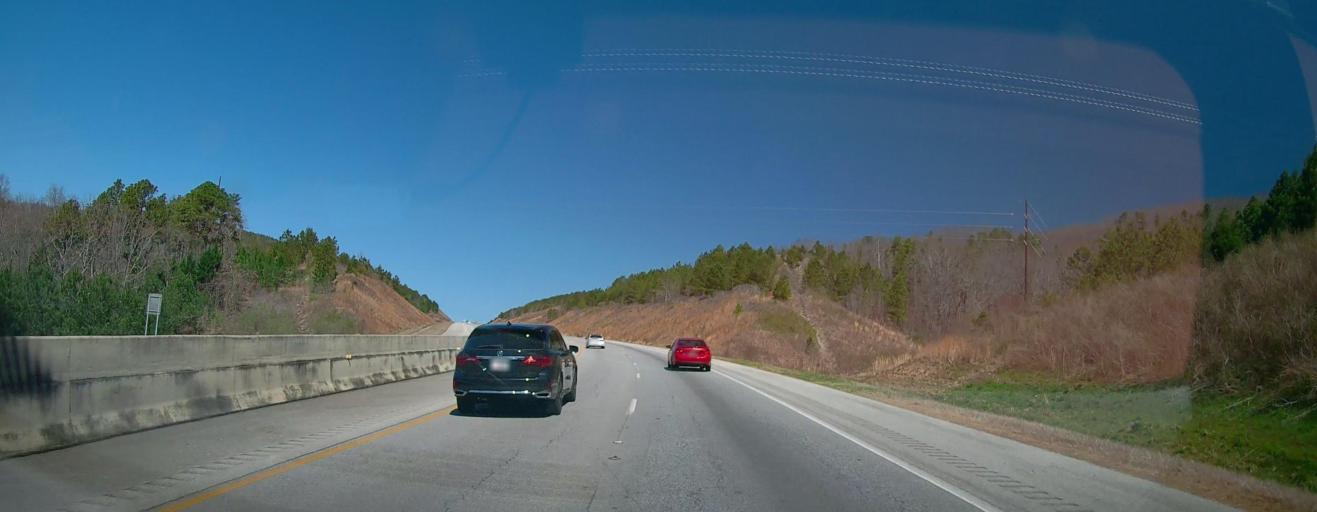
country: US
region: Alabama
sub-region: Calhoun County
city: Anniston
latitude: 33.6557
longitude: -85.7844
